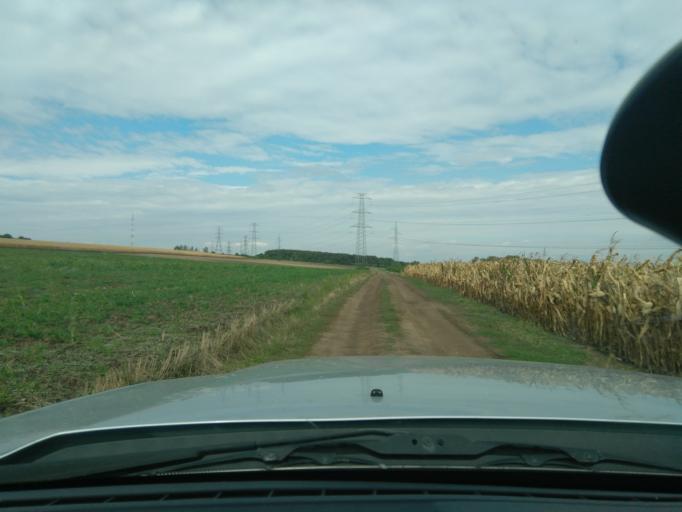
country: HU
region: Fejer
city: Val
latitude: 47.3727
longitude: 18.6962
